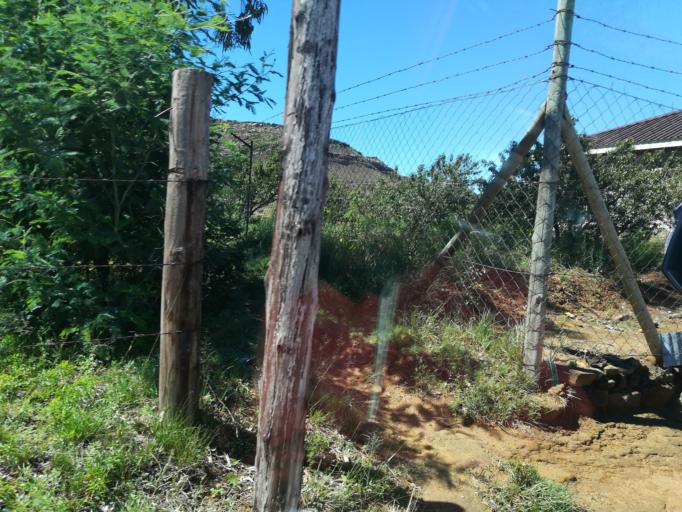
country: LS
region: Quthing
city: Quthing
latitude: -30.3307
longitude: 27.5317
